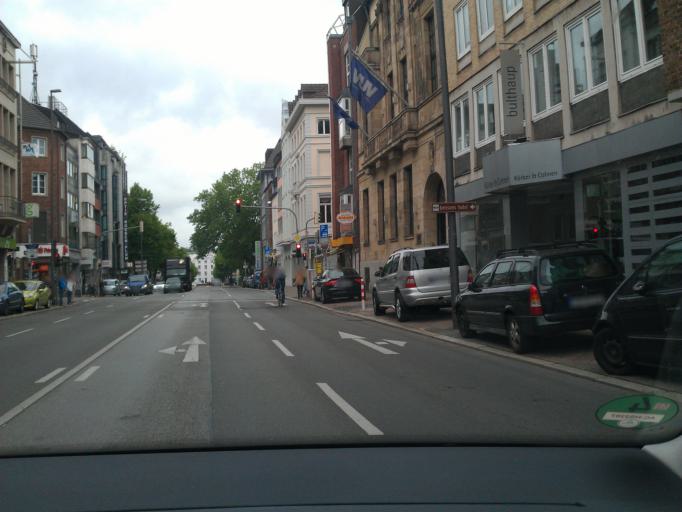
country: DE
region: North Rhine-Westphalia
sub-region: Regierungsbezirk Koln
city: Aachen
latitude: 50.7704
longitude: 6.0928
